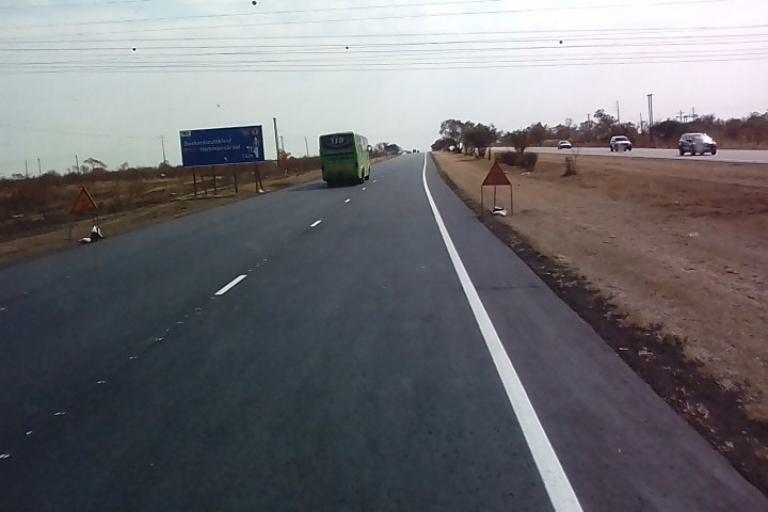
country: ZA
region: Gauteng
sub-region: City of Tshwane Metropolitan Municipality
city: Mabopane
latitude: -25.4187
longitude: 28.2970
